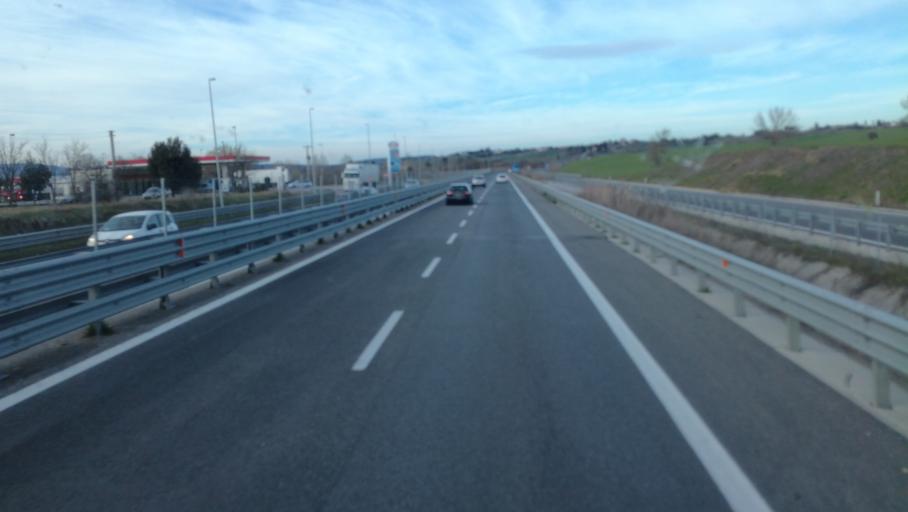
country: IT
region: Tuscany
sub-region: Provincia di Siena
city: Rosia
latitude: 43.2302
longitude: 11.2761
